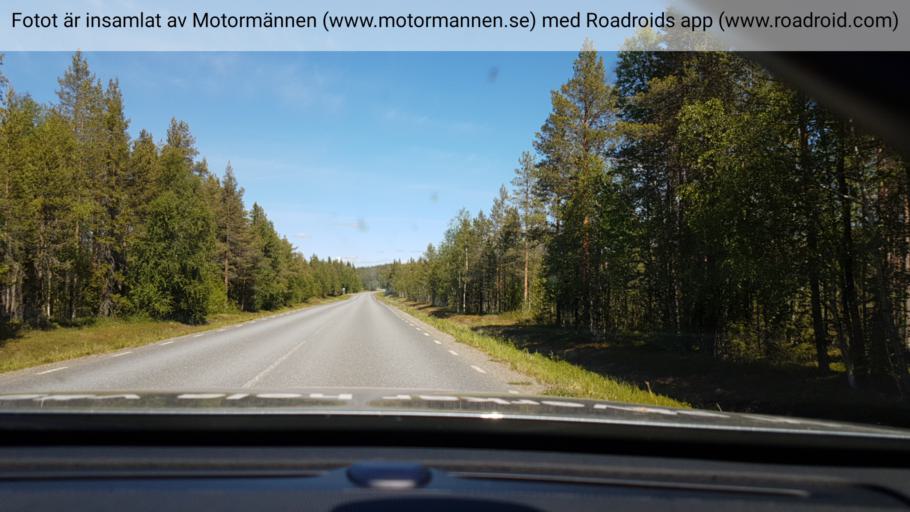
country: SE
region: Vaesterbotten
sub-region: Vilhelmina Kommun
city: Vilhelmina
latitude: 64.6544
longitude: 17.0859
